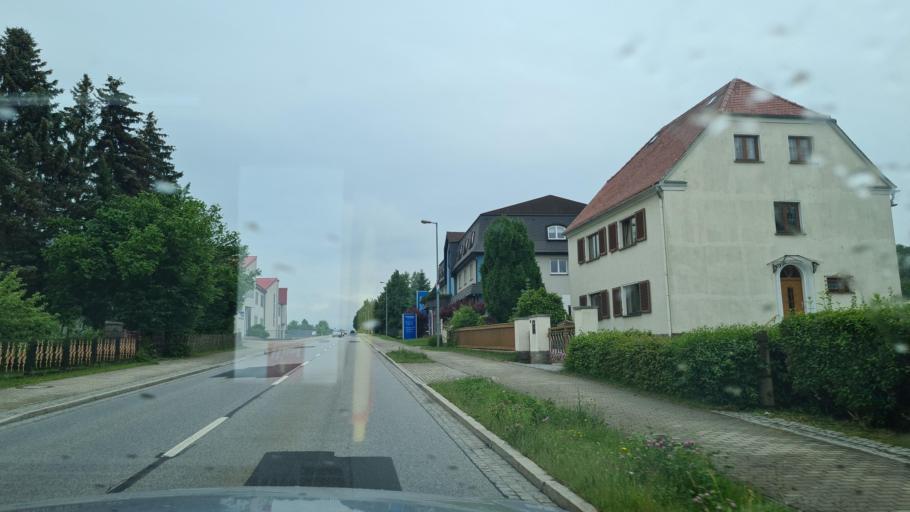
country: DE
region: Saxony
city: Grosspostwitz
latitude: 51.1131
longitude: 14.4455
